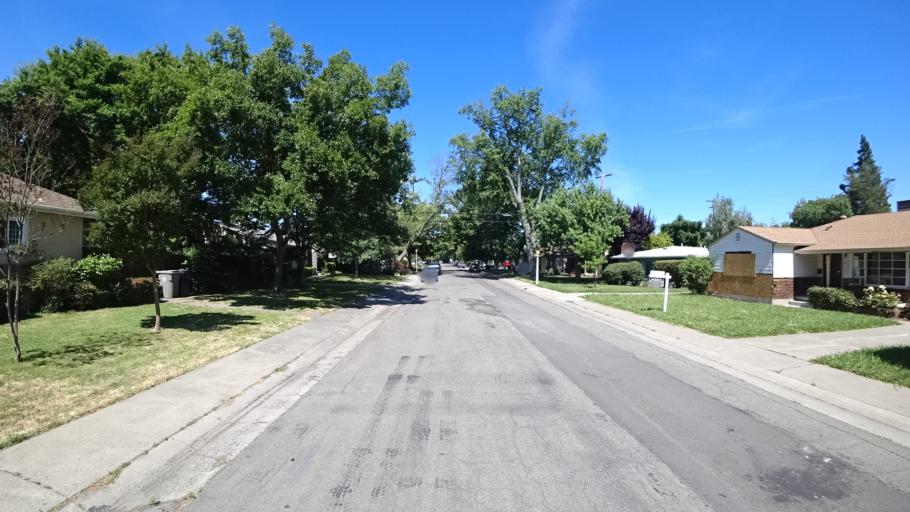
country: US
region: California
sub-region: Sacramento County
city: Sacramento
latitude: 38.5579
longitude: -121.5066
